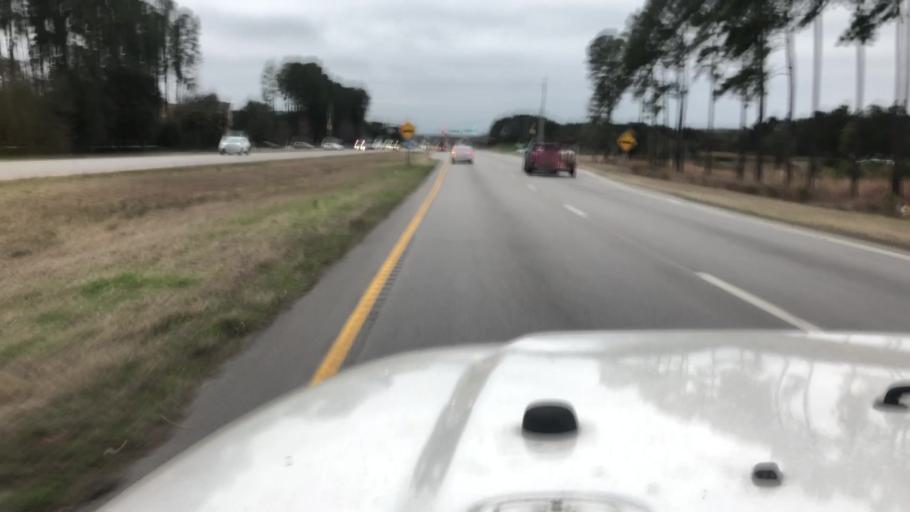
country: US
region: South Carolina
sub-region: Beaufort County
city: Bluffton
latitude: 32.2984
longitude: -80.9450
